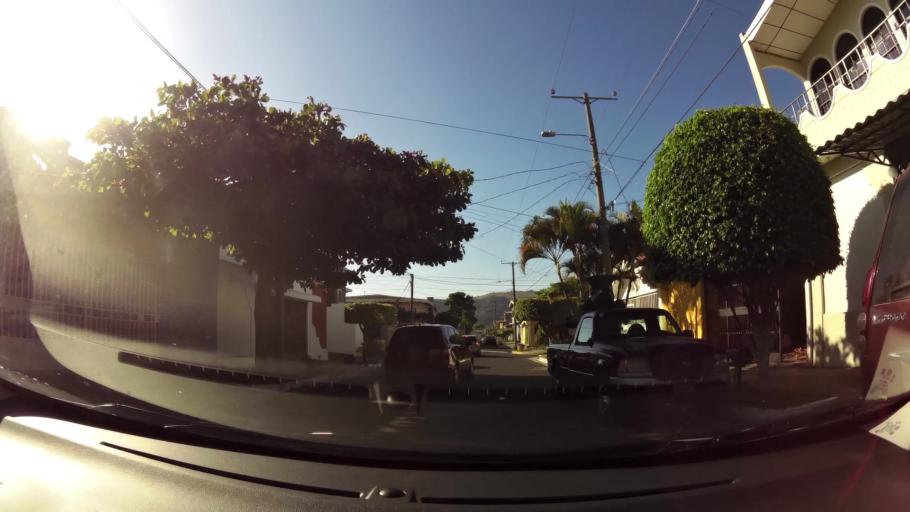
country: SV
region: La Libertad
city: Santa Tecla
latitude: 13.6810
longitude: -89.2900
